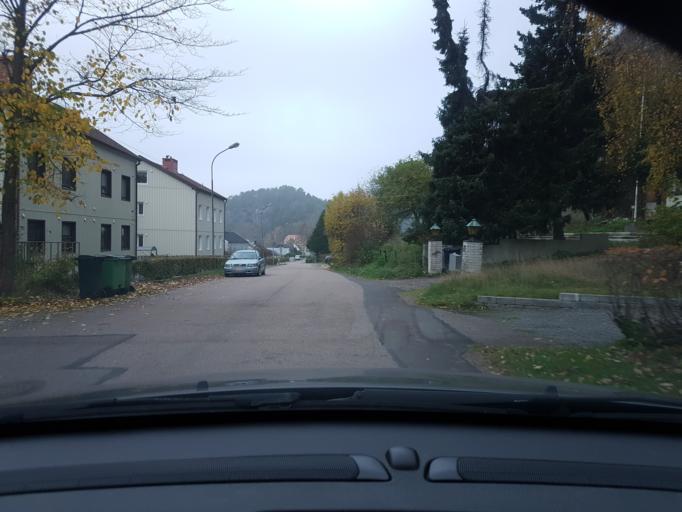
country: SE
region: Vaestra Goetaland
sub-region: Ale Kommun
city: Surte
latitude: 57.8353
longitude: 12.0204
